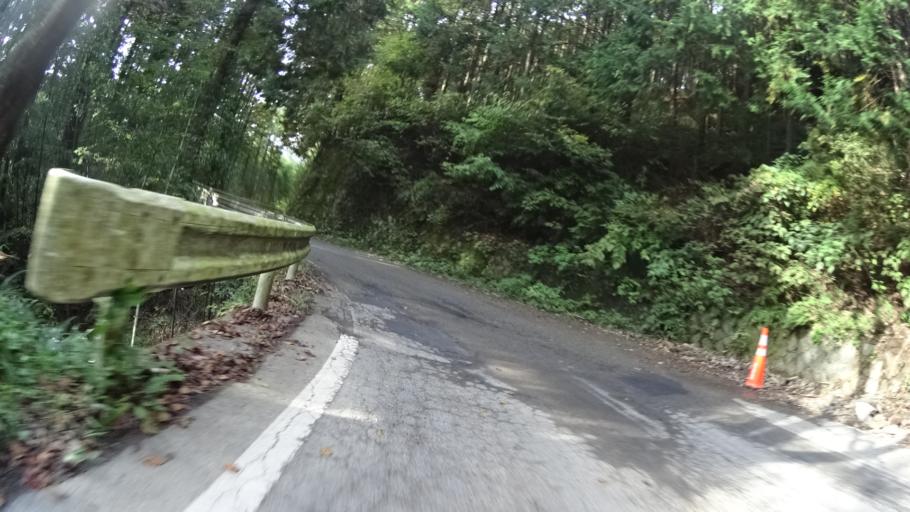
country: JP
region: Yamanashi
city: Uenohara
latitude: 35.6781
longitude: 139.0958
